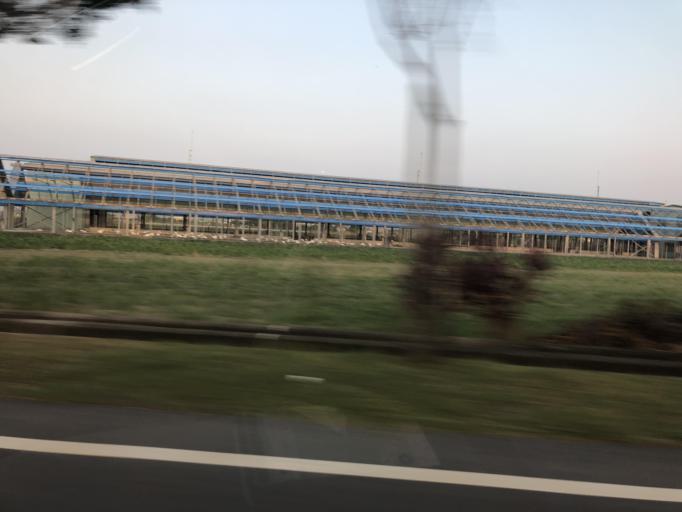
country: TW
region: Taiwan
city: Xinying
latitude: 23.2380
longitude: 120.2737
